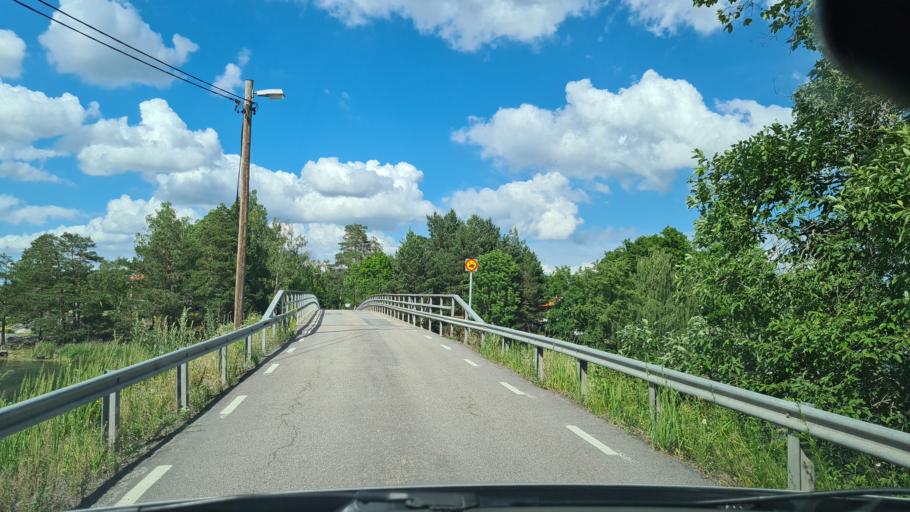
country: SE
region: Stockholm
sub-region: Vaxholms Kommun
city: Vaxholm
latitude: 59.4074
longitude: 18.3688
